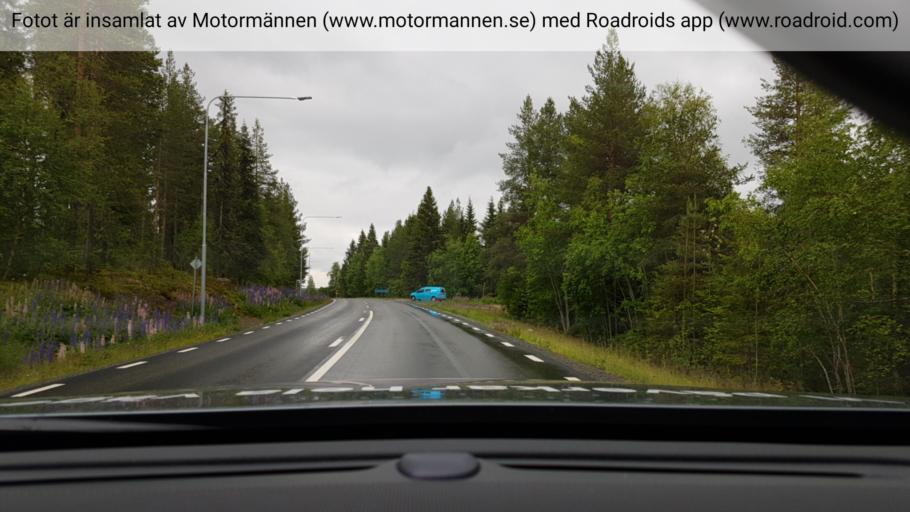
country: SE
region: Vaesterbotten
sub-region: Norsjo Kommun
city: Norsjoe
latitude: 65.2662
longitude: 19.6126
